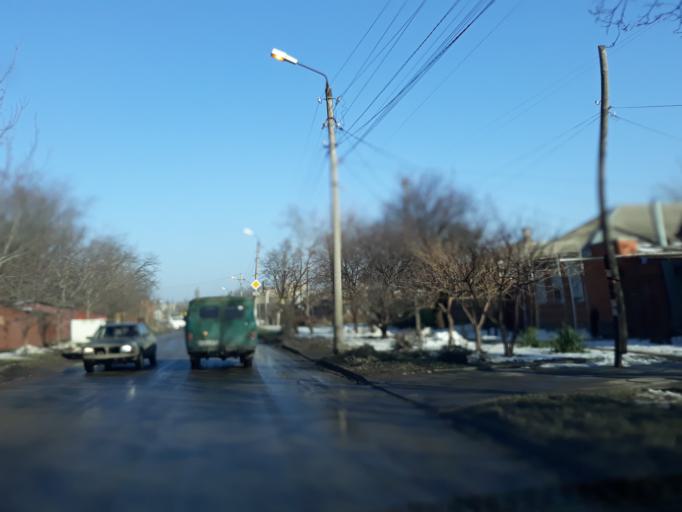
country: RU
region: Rostov
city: Taganrog
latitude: 47.2266
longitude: 38.8762
